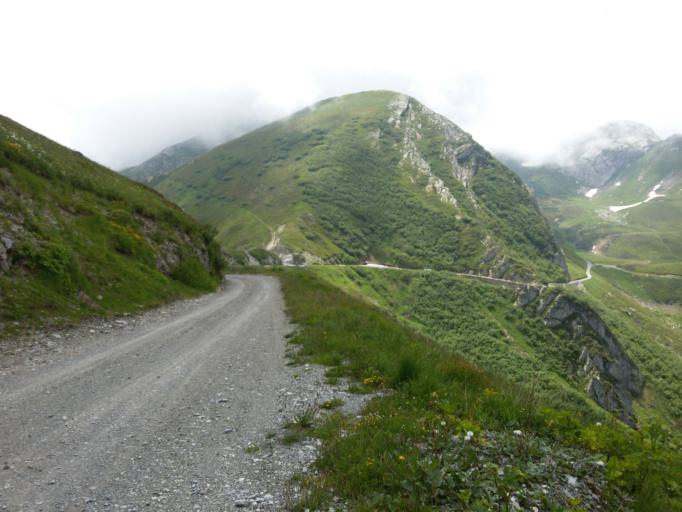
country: IT
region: Piedmont
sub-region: Provincia di Cuneo
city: Limone Piemonte
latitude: 44.1576
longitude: 7.6255
